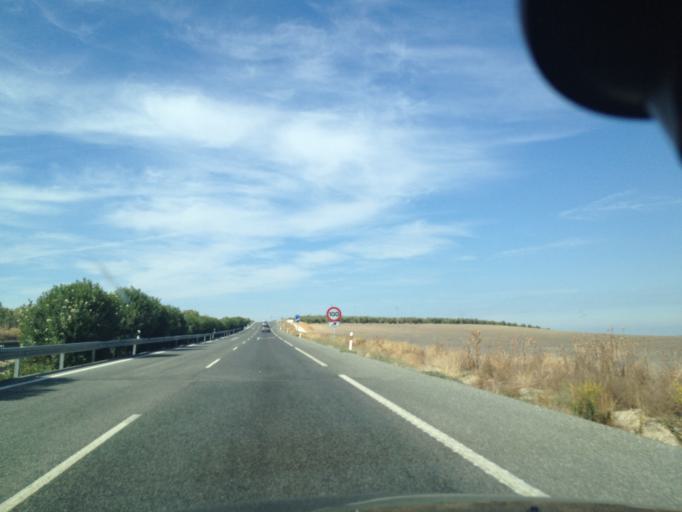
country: ES
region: Andalusia
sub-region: Provincia de Sevilla
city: Osuna
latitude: 37.2328
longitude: -5.2048
